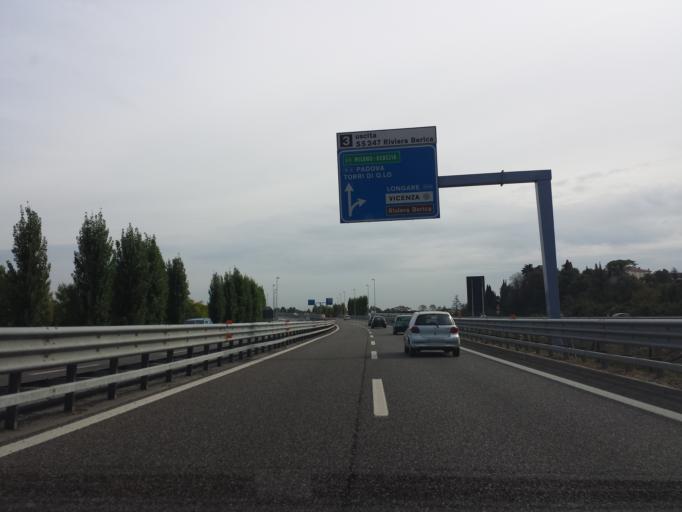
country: IT
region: Veneto
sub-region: Provincia di Vicenza
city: Arcugnano-Torri
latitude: 45.5160
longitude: 11.5567
